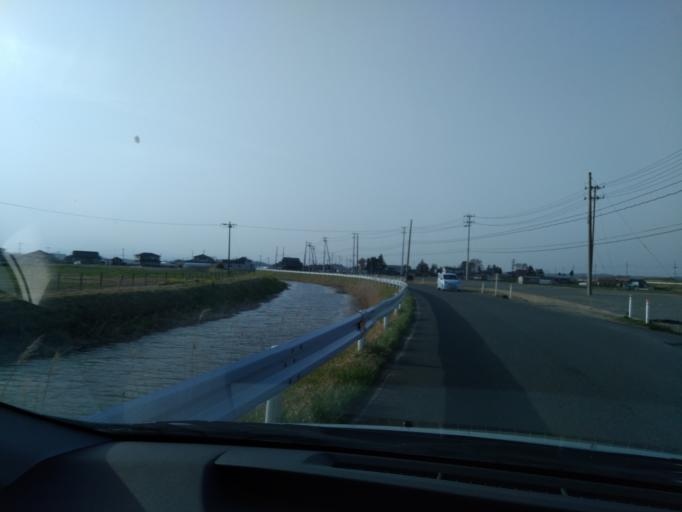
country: JP
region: Iwate
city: Ichinoseki
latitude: 38.7548
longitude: 141.1347
